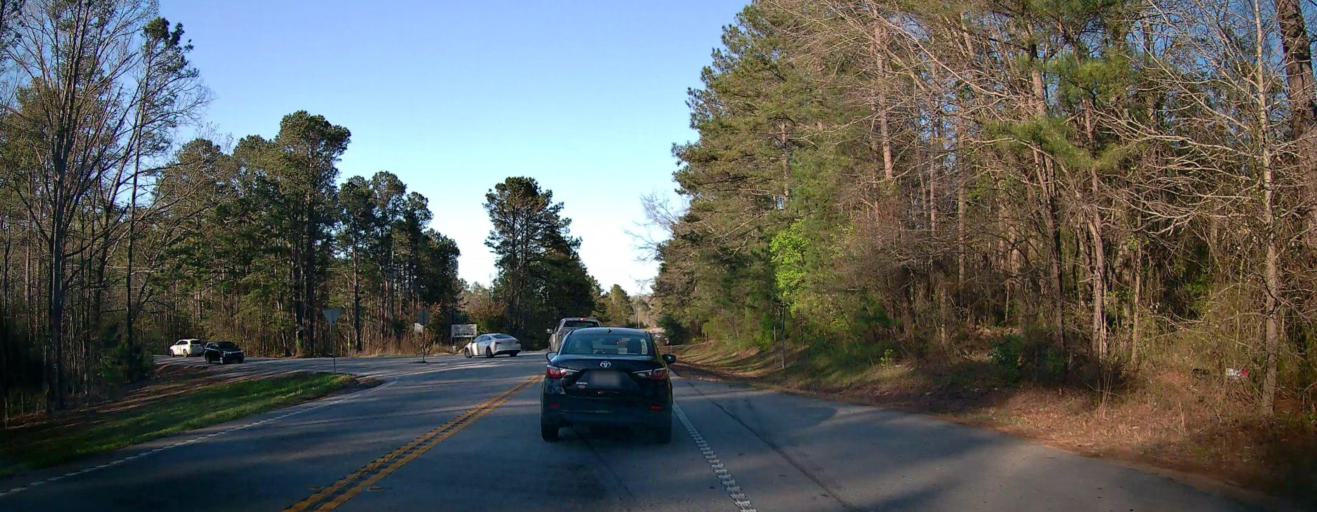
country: US
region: Georgia
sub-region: Butts County
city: Jackson
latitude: 33.4044
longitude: -83.8865
